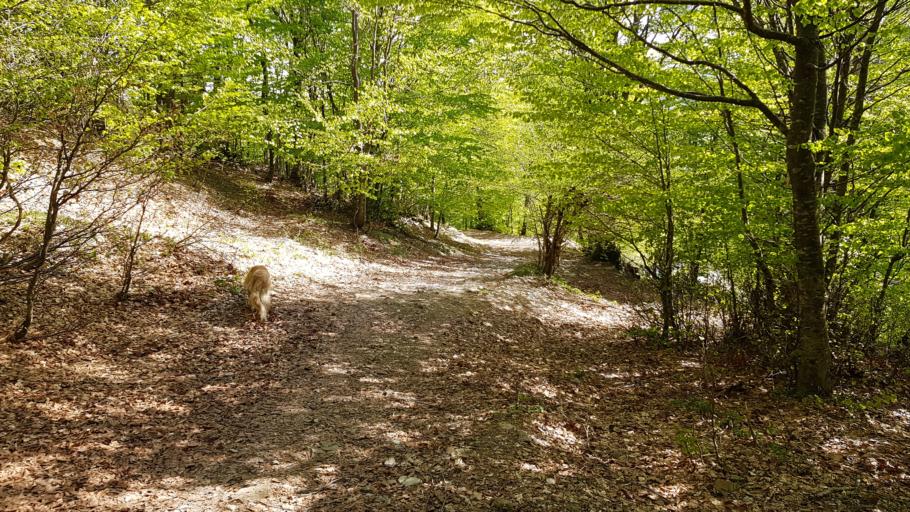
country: IT
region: Liguria
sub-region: Provincia di Genova
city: Fascia
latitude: 44.6065
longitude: 9.2039
